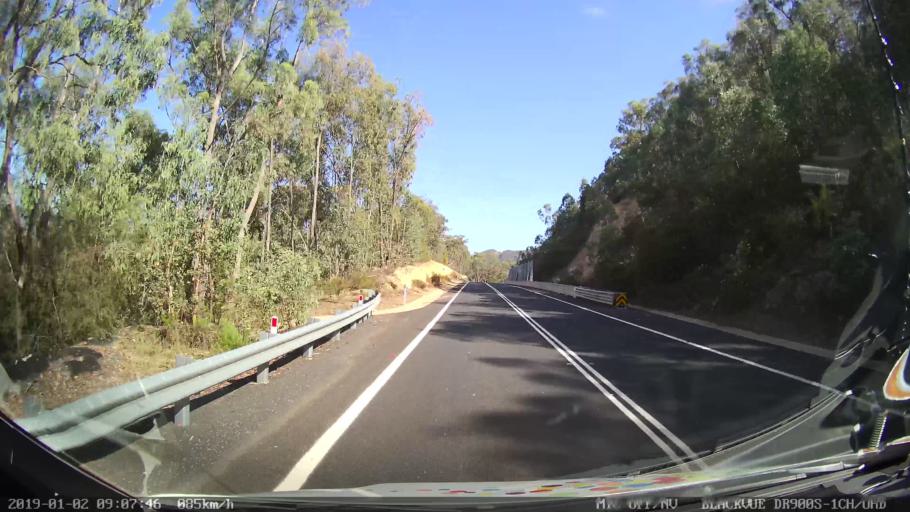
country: AU
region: New South Wales
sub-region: Tumut Shire
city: Tumut
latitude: -35.5372
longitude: 148.2962
